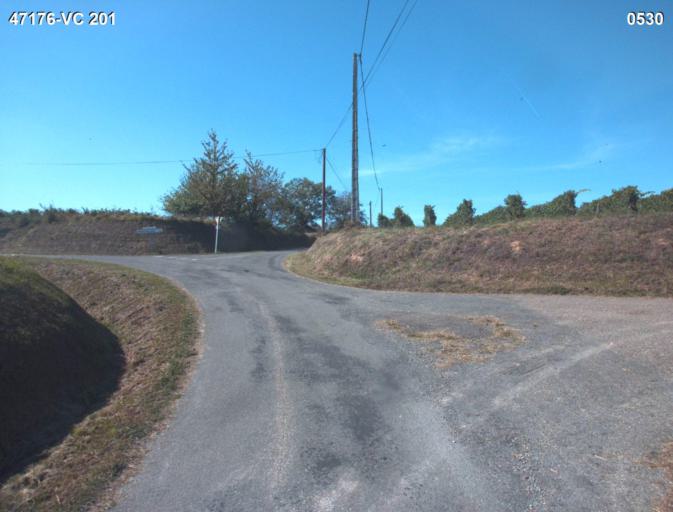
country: FR
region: Aquitaine
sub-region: Departement du Lot-et-Garonne
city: Vianne
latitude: 44.2118
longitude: 0.3079
